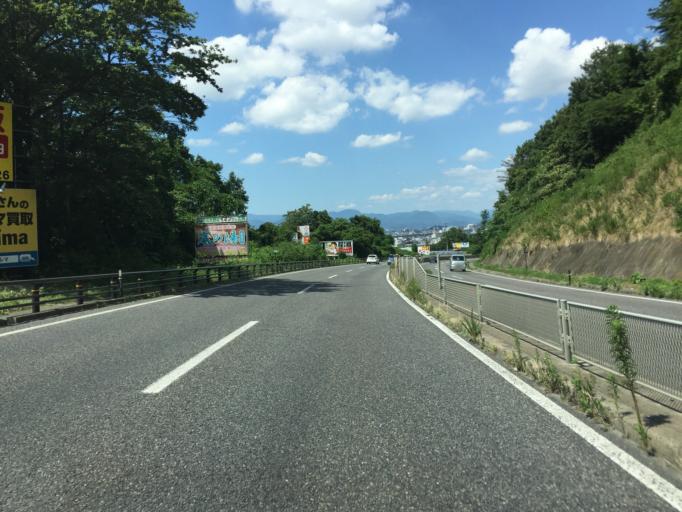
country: JP
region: Fukushima
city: Fukushima-shi
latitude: 37.7171
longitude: 140.4656
